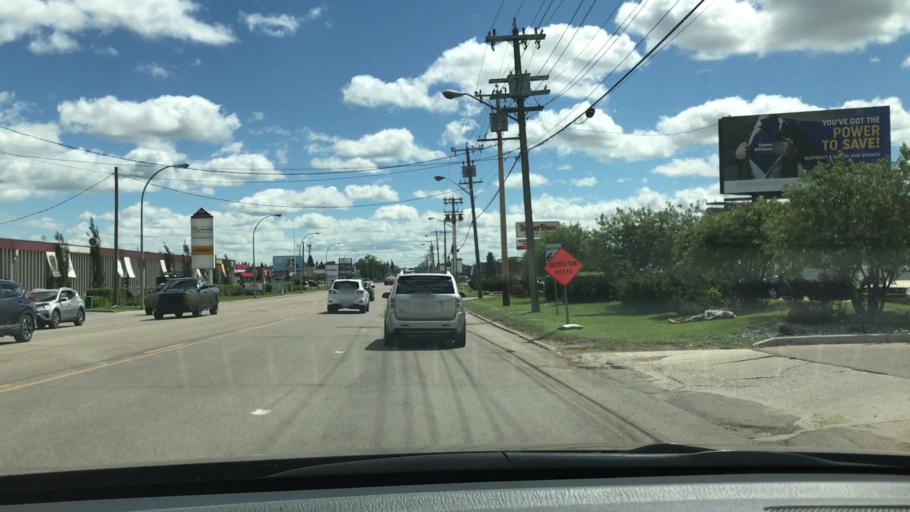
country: CA
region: Alberta
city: Edmonton
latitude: 53.4873
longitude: -113.4862
